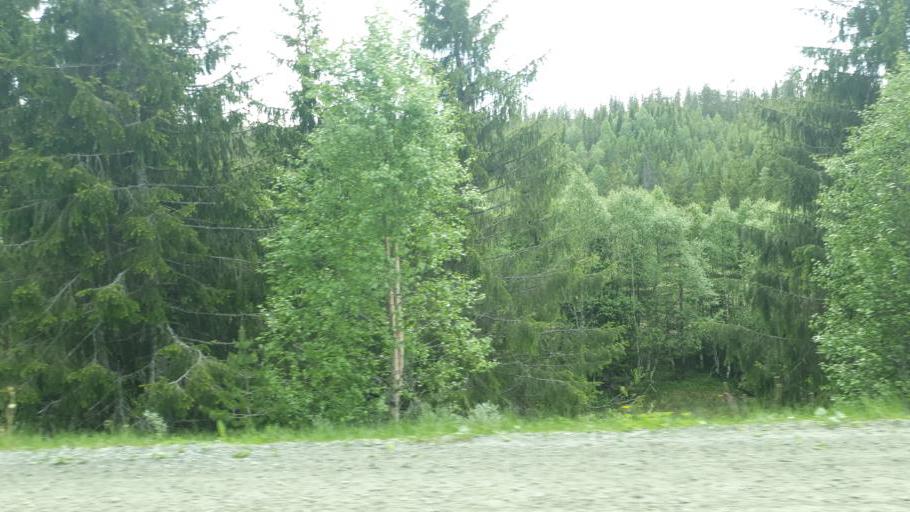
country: NO
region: Sor-Trondelag
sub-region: Trondheim
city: Trondheim
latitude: 63.6805
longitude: 10.3548
